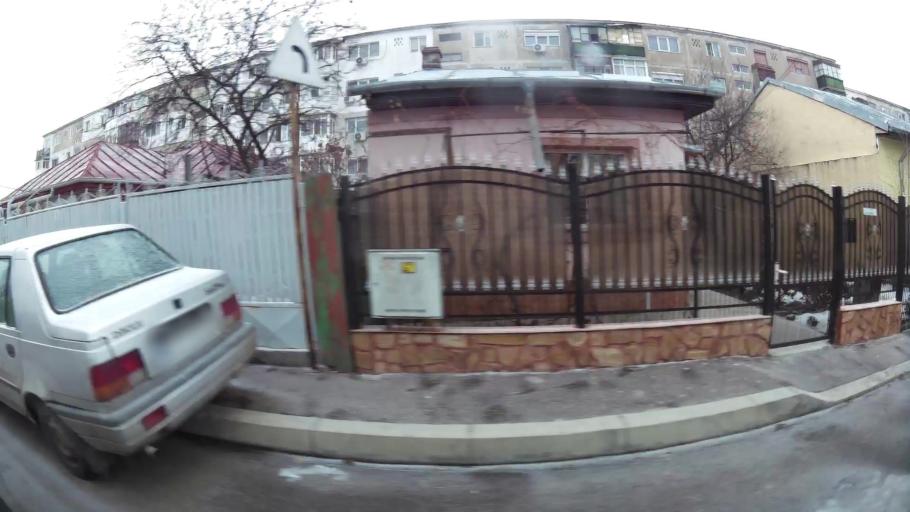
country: RO
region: Prahova
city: Ploiesti
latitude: 44.9401
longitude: 26.0437
